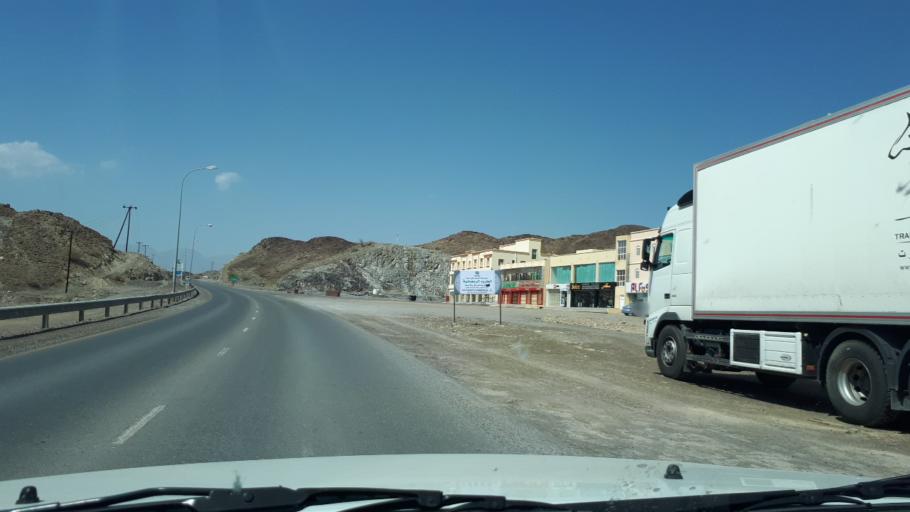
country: OM
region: Muhafazat ad Dakhiliyah
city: Bahla'
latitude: 22.9510
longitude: 57.2865
